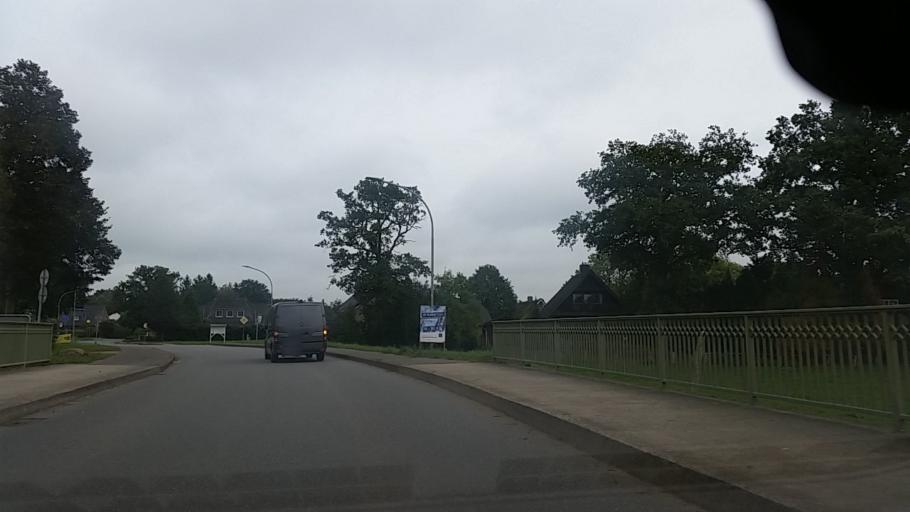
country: DE
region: Schleswig-Holstein
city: Schmalfeld
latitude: 53.8806
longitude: 9.9825
